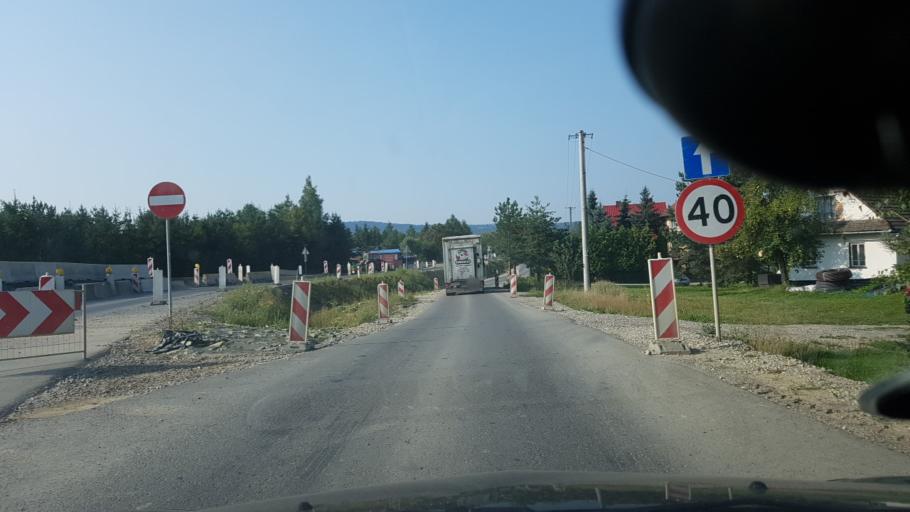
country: PL
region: Lesser Poland Voivodeship
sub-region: Powiat nowotarski
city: Rokiciny
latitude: 49.6033
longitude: 19.9238
